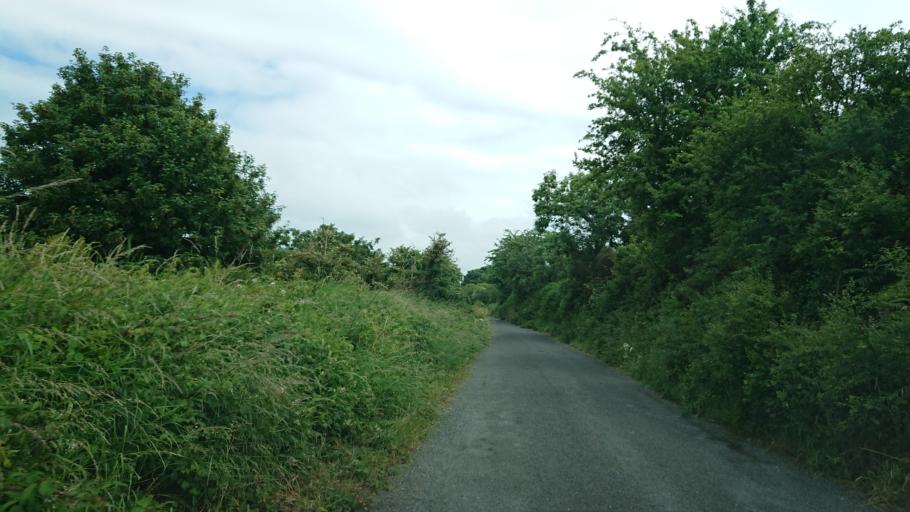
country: IE
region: Munster
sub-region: Waterford
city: Waterford
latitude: 52.2717
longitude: -7.1427
